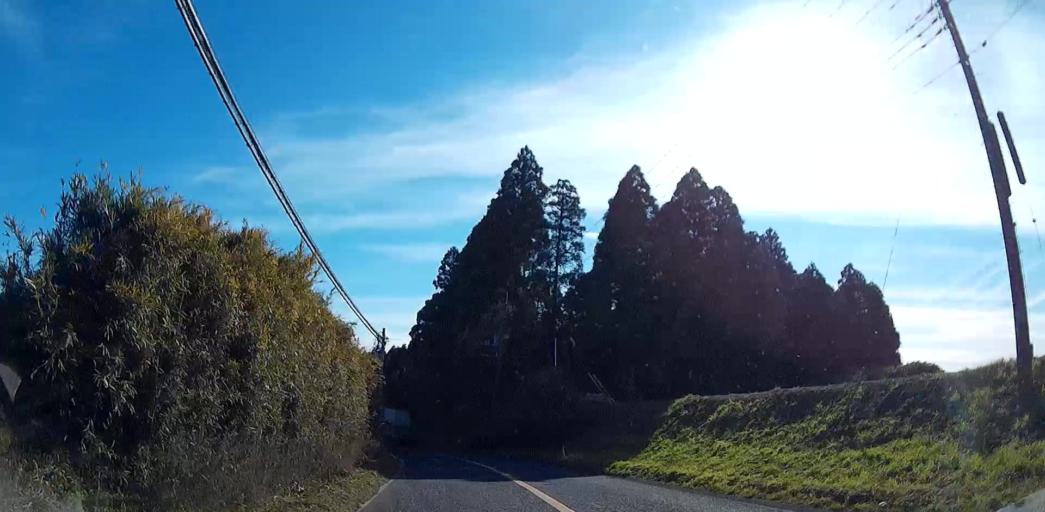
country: JP
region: Chiba
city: Yokaichiba
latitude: 35.7638
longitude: 140.4460
